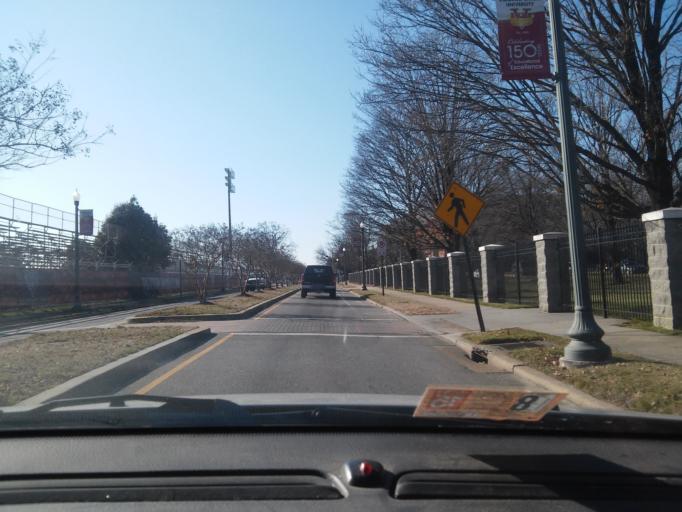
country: US
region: Virginia
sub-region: City of Richmond
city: Richmond
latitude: 37.5620
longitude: -77.4488
